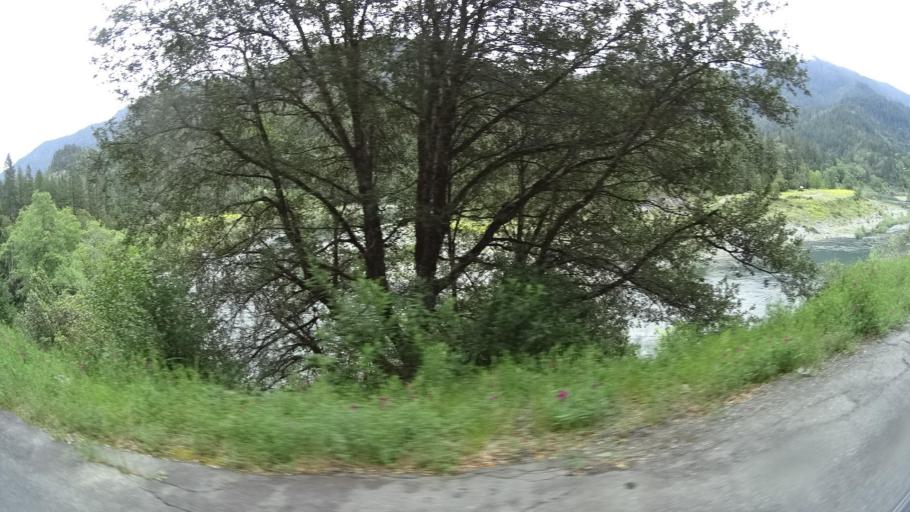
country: US
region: California
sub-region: Humboldt County
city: Willow Creek
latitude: 41.3189
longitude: -123.5289
